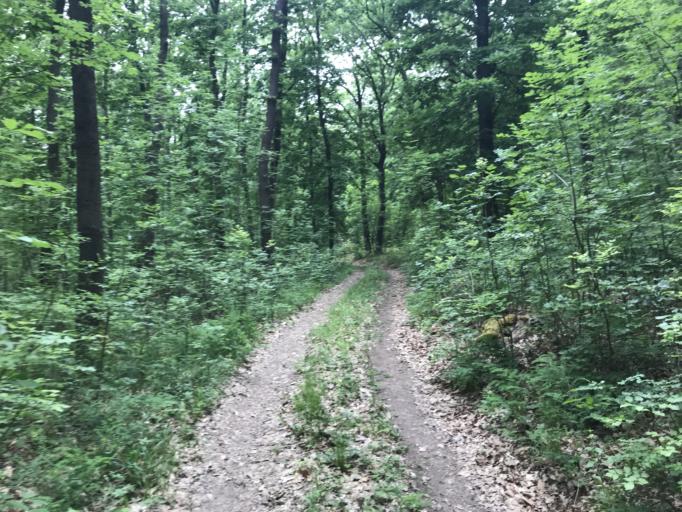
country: HU
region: Pest
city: Csobanka
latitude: 47.6562
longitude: 18.9316
